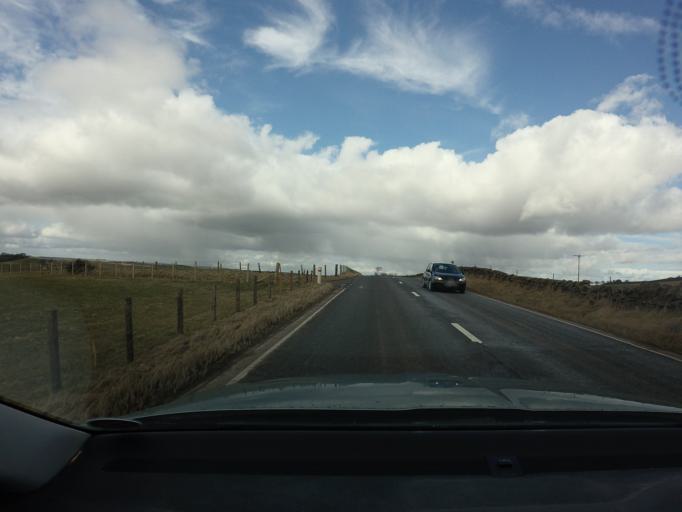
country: GB
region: Scotland
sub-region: South Lanarkshire
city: Lanark
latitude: 55.6319
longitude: -3.7446
